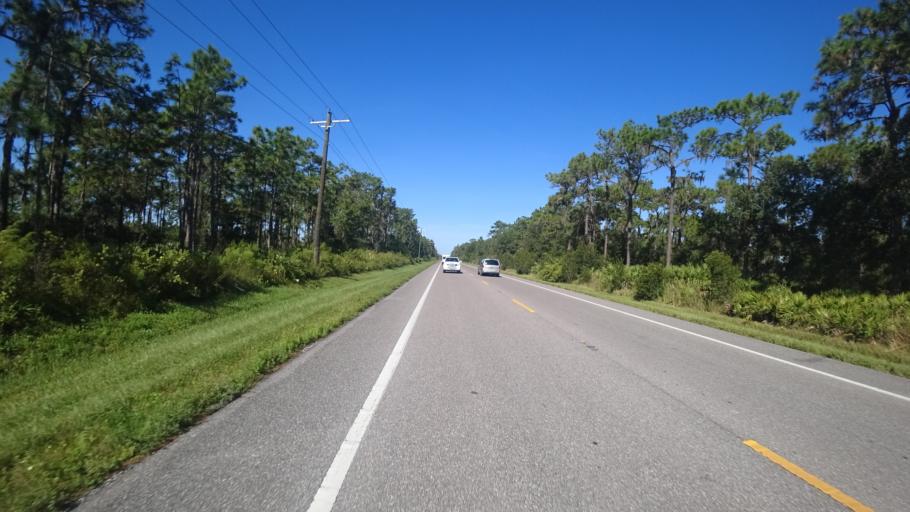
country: US
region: Florida
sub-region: Sarasota County
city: Lake Sarasota
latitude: 27.3906
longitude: -82.2863
